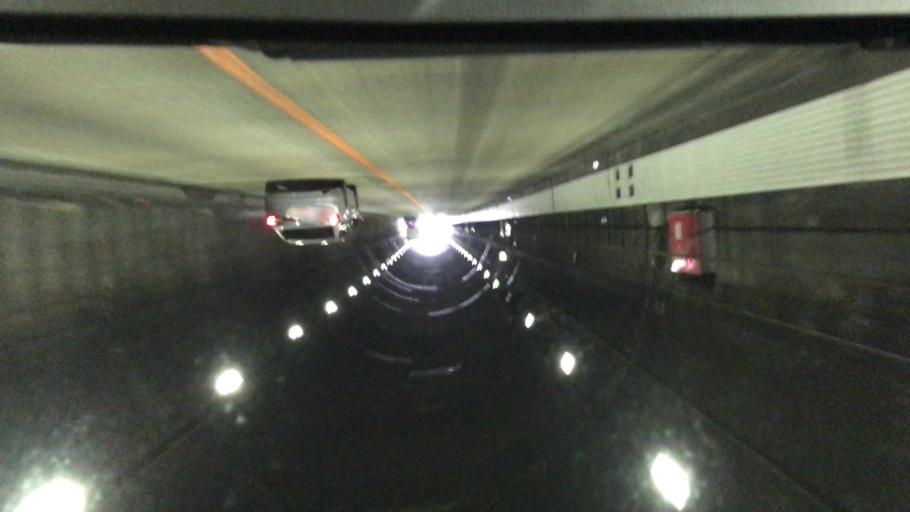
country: JP
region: Yamaguchi
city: Tokuyama
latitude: 34.0827
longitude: 131.7376
